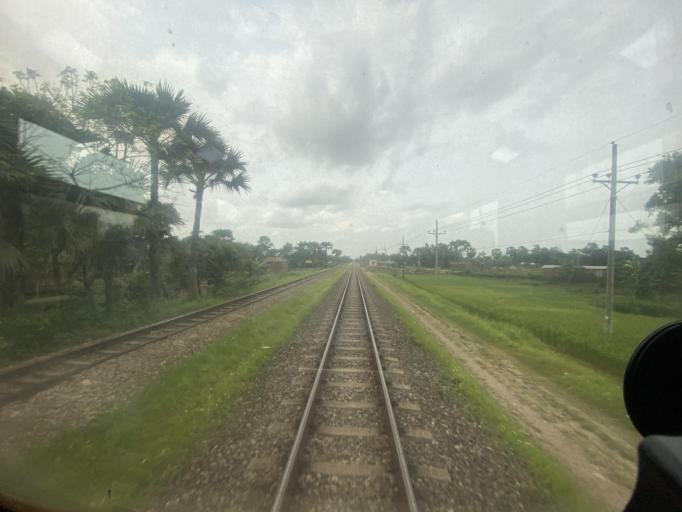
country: BD
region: Chittagong
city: Laksham
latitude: 23.2070
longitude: 91.1520
